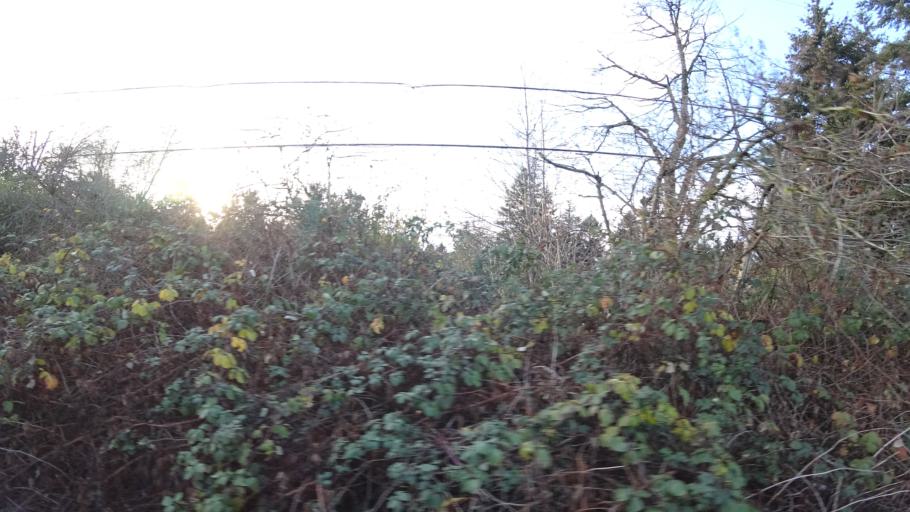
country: US
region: Oregon
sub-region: Multnomah County
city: Lents
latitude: 45.5167
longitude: -122.5452
